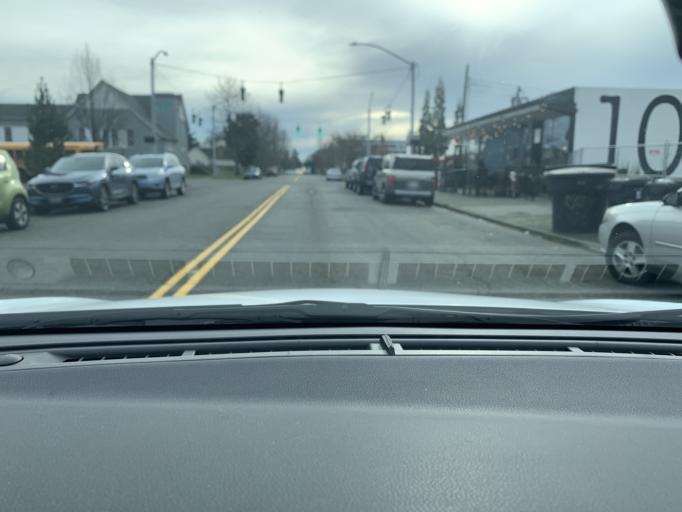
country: US
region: Washington
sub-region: Pierce County
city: Tacoma
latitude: 47.2526
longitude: -122.4504
